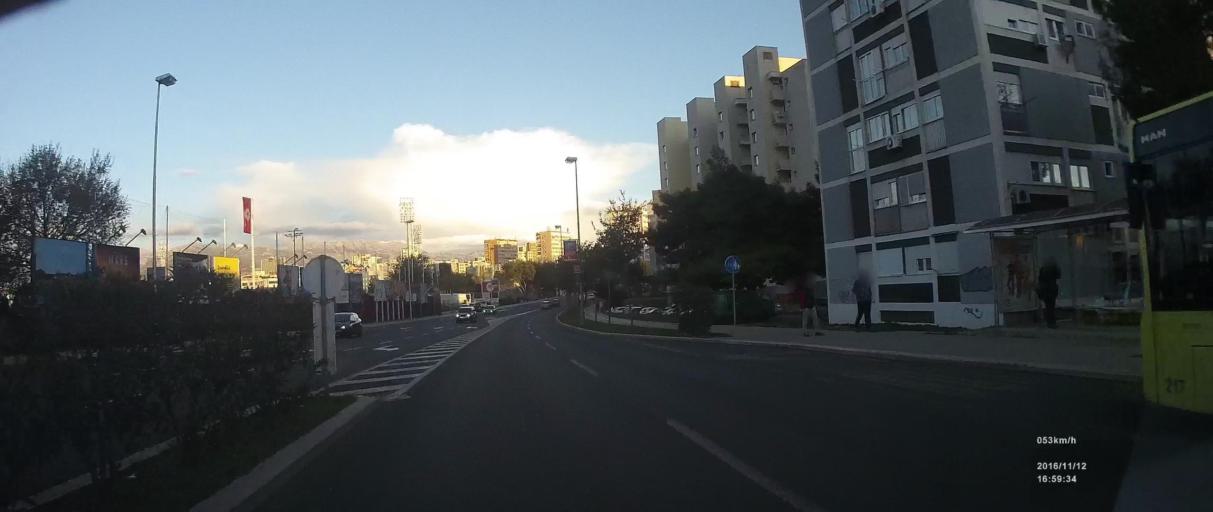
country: HR
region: Splitsko-Dalmatinska
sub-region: Grad Split
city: Split
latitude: 43.5186
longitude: 16.4404
